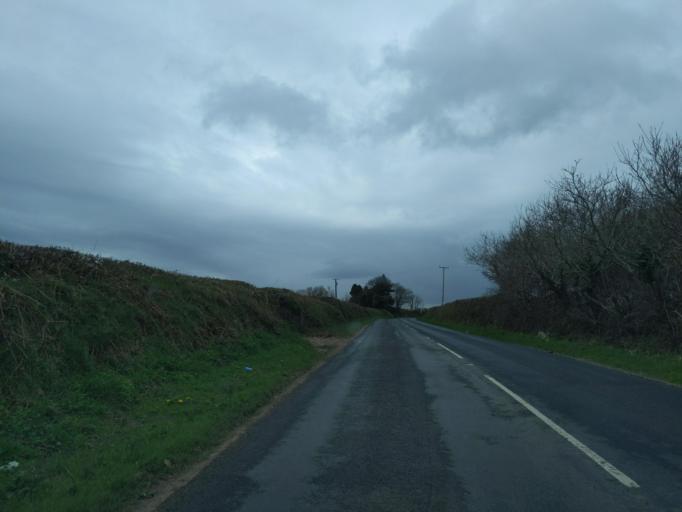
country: GB
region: England
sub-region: Cornwall
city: South Hill
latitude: 50.5472
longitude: -4.3682
